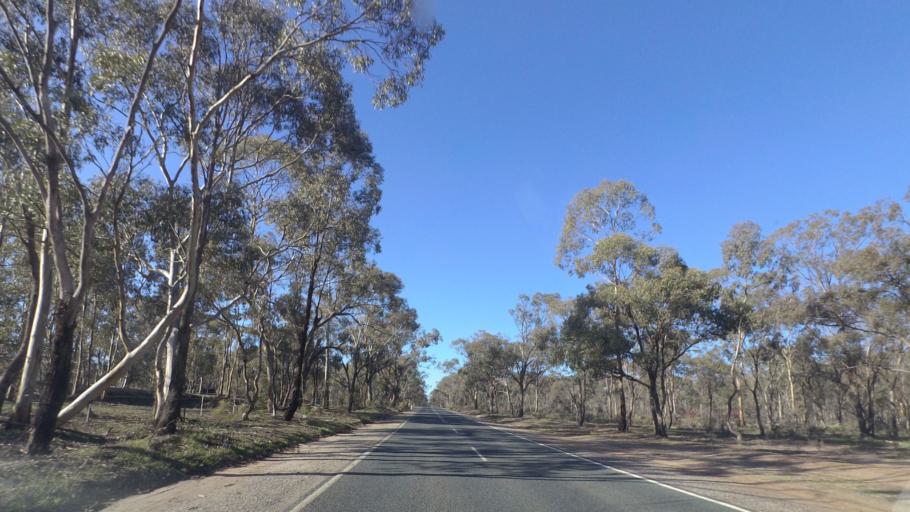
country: AU
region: Victoria
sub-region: Greater Bendigo
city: Epsom
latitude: -36.6736
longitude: 144.4031
